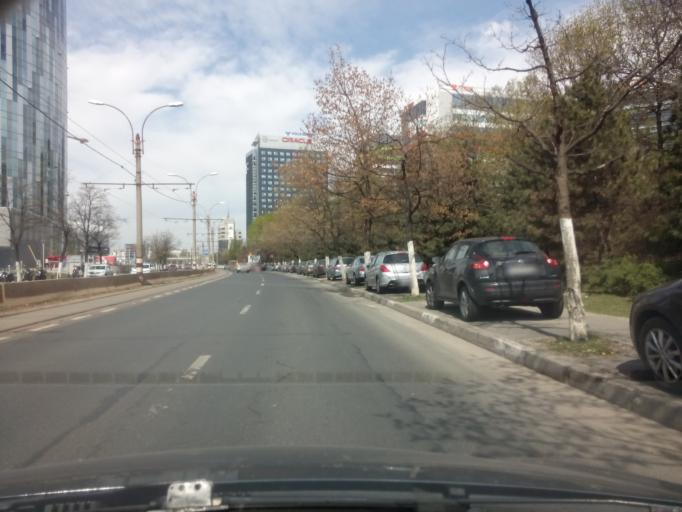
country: RO
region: Bucuresti
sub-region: Municipiul Bucuresti
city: Bucharest
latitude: 44.4772
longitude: 26.1062
